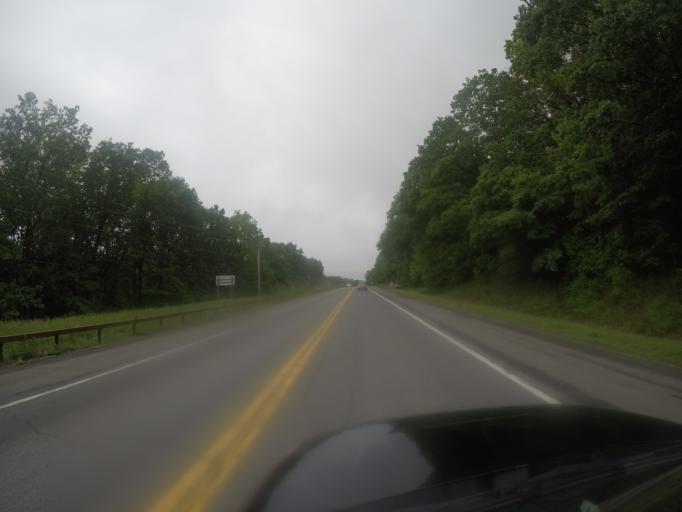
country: US
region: New York
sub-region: Ulster County
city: West Hurley
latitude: 41.9961
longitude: -74.1544
